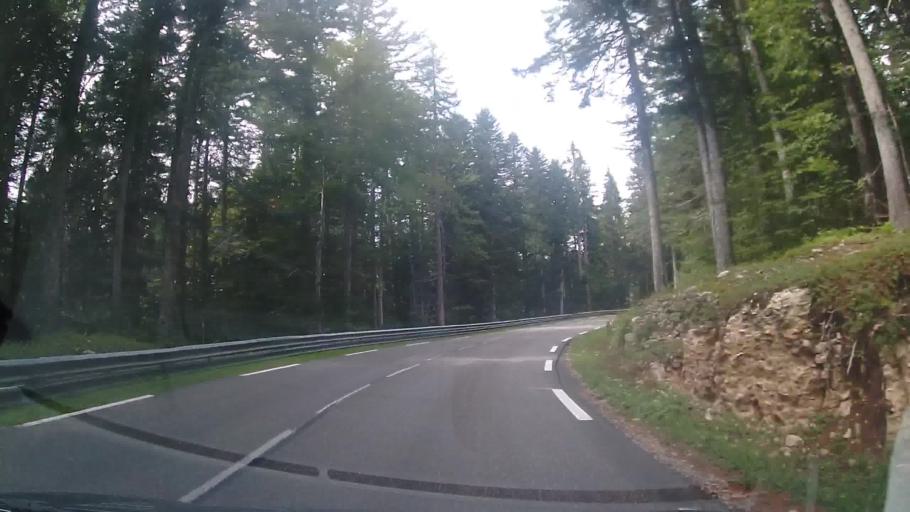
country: FR
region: Rhone-Alpes
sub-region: Departement de l'Ain
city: Gex
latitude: 46.3945
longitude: 6.0488
